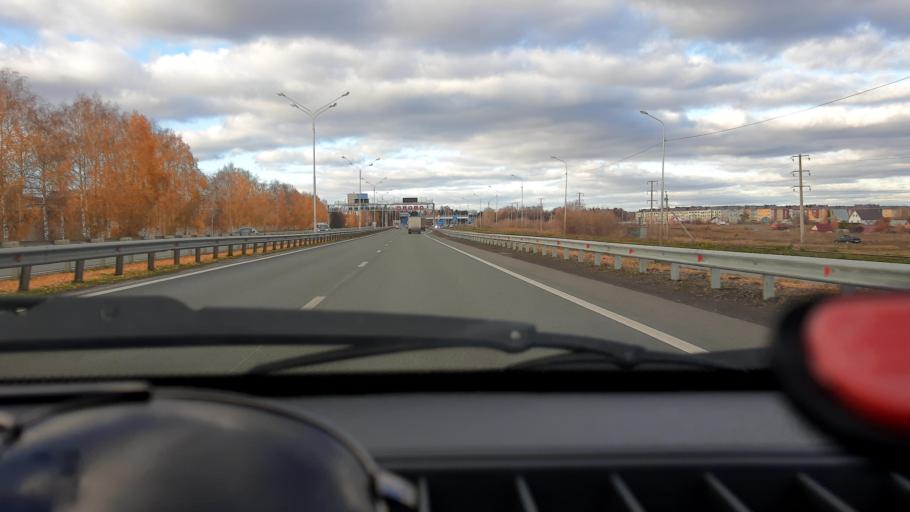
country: RU
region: Bashkortostan
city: Ufa
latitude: 54.5832
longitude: 55.9131
